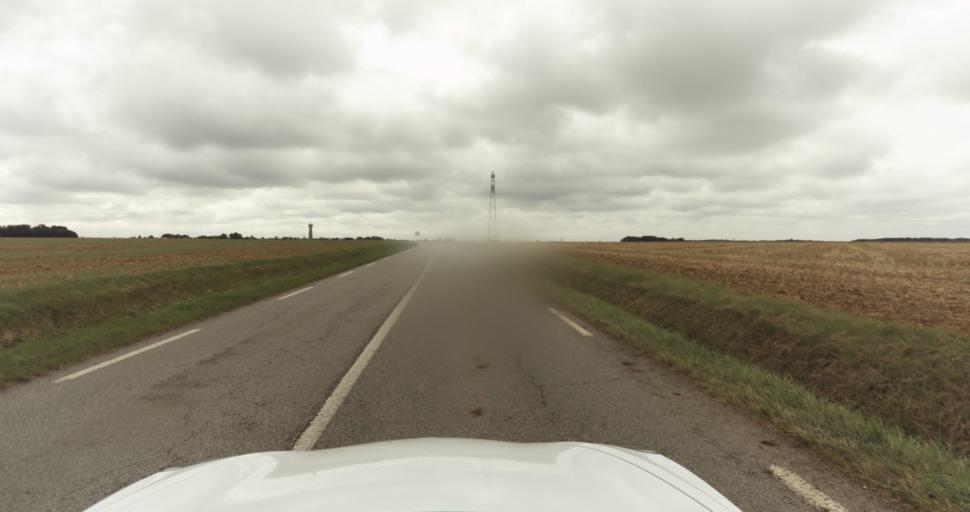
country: FR
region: Haute-Normandie
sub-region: Departement de l'Eure
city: Aviron
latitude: 49.0431
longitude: 1.0874
